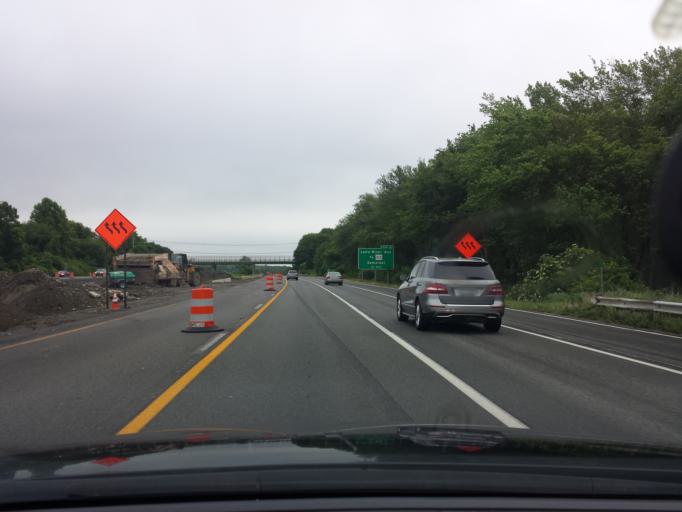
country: US
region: Massachusetts
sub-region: Bristol County
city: Ocean Grove
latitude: 41.7344
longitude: -71.2004
